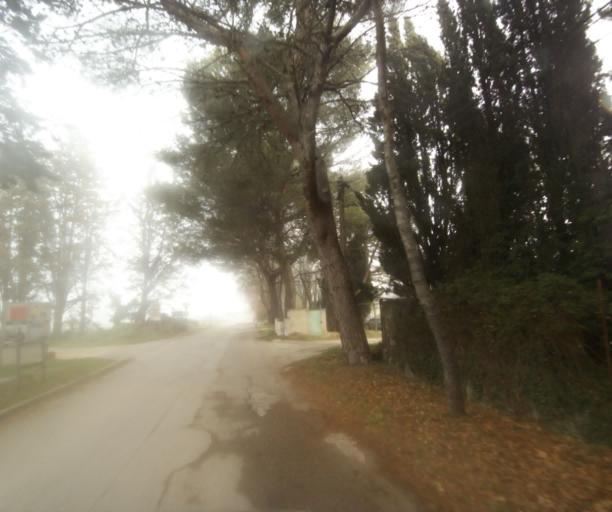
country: FR
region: Provence-Alpes-Cote d'Azur
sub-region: Departement des Bouches-du-Rhone
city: Eguilles
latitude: 43.5447
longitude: 5.3568
